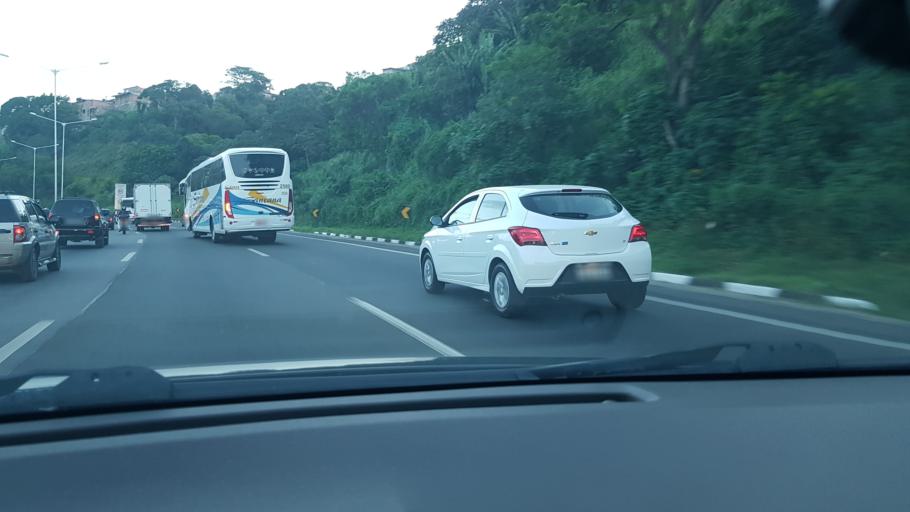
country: BR
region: Bahia
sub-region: Salvador
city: Salvador
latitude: -12.9355
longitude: -38.4724
